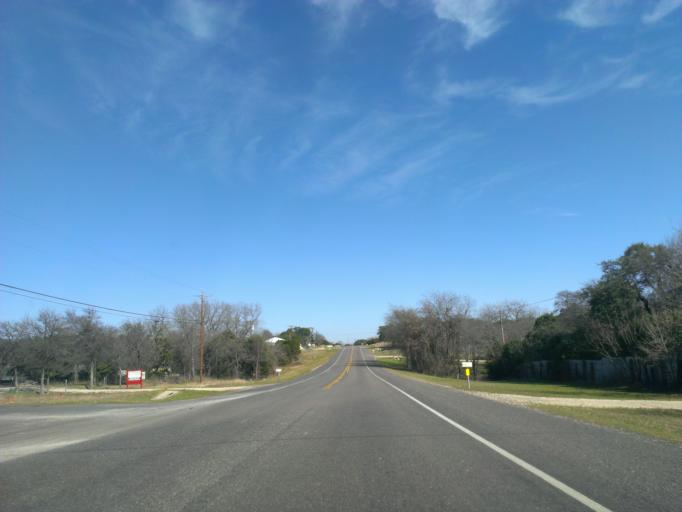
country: US
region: Texas
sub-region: Bell County
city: Belton
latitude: 31.0404
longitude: -97.5209
